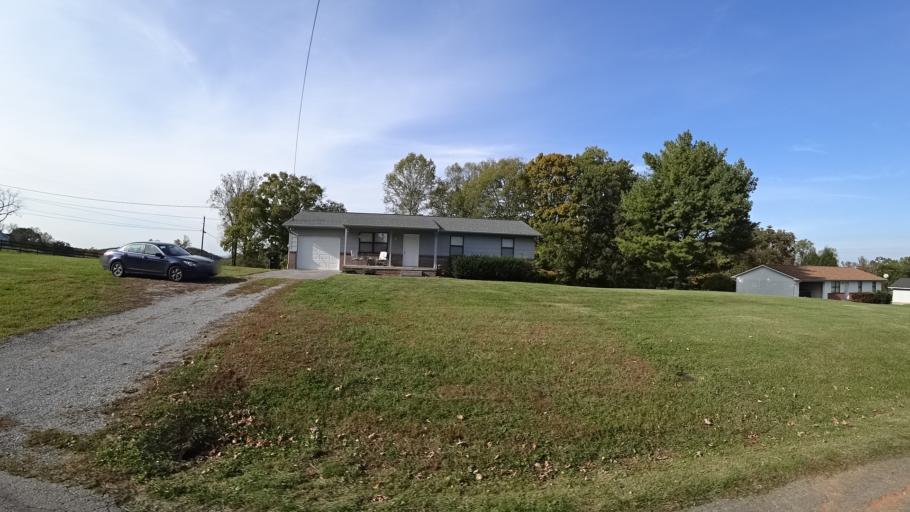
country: US
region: Tennessee
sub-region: Knox County
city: Farragut
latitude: 35.9113
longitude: -84.1745
